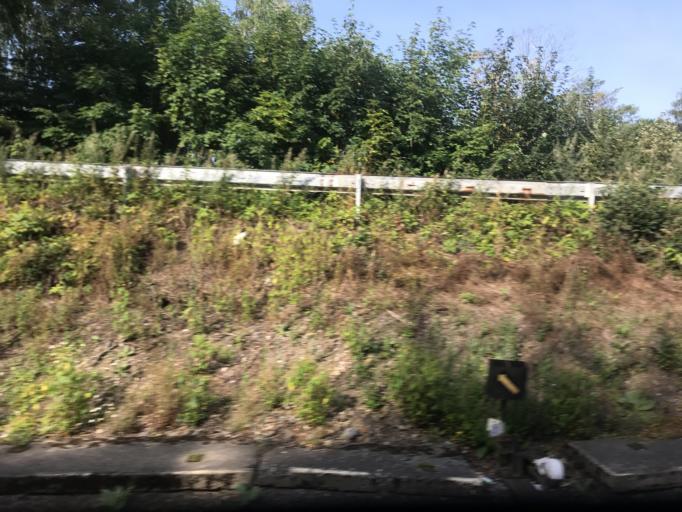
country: CZ
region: Jihocesky
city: Chotoviny
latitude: 49.5373
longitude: 14.6221
